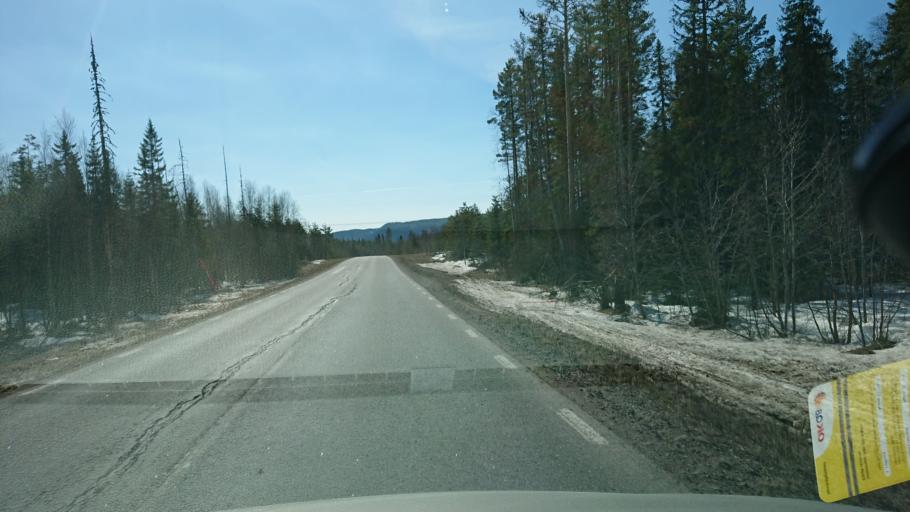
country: SE
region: Vaesternorrland
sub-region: Solleftea Kommun
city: As
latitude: 63.5834
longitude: 16.4360
